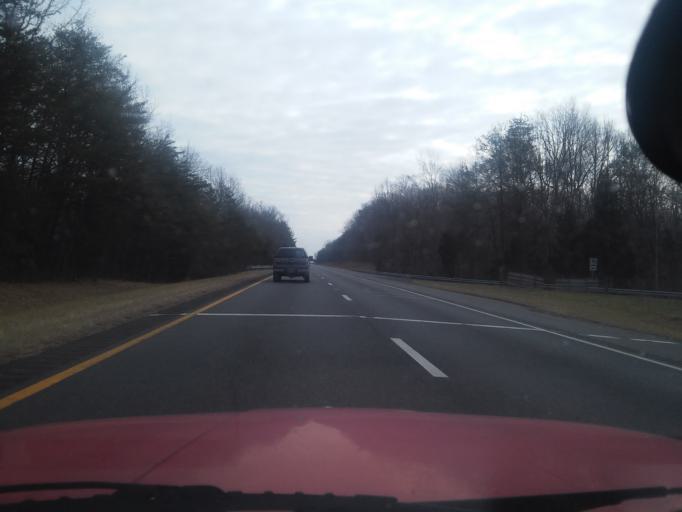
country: US
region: Virginia
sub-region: Louisa County
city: Louisa
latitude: 37.9091
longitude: -78.0622
